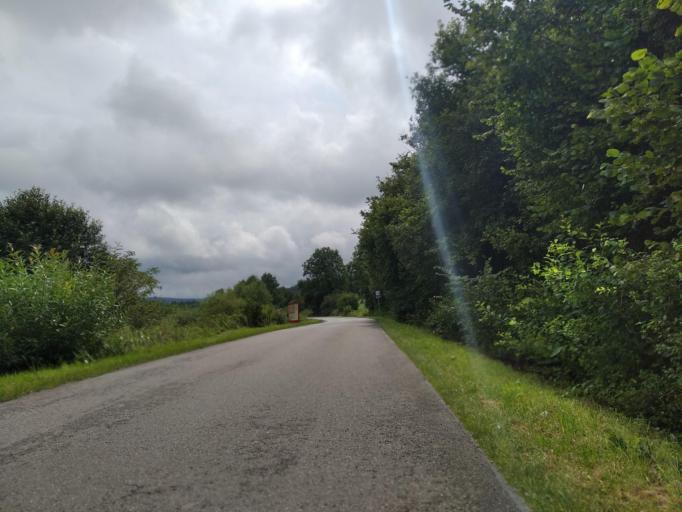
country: PL
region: Subcarpathian Voivodeship
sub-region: Powiat brzozowski
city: Nozdrzec
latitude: 49.7416
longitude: 22.2422
